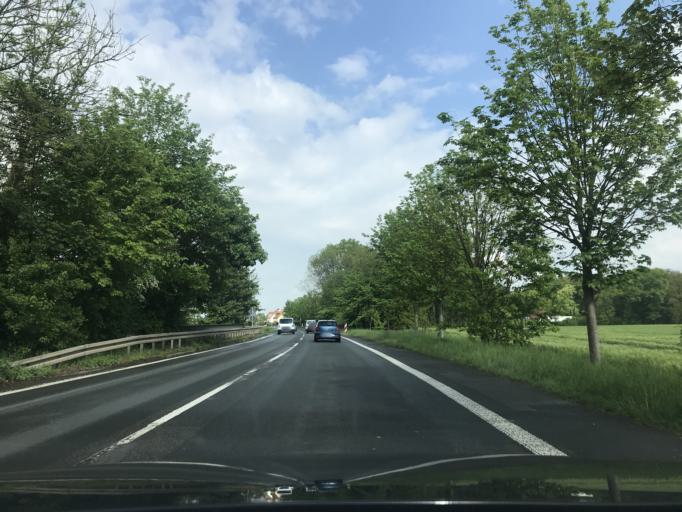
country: DE
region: North Rhine-Westphalia
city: Schwerte
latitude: 51.4246
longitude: 7.5496
